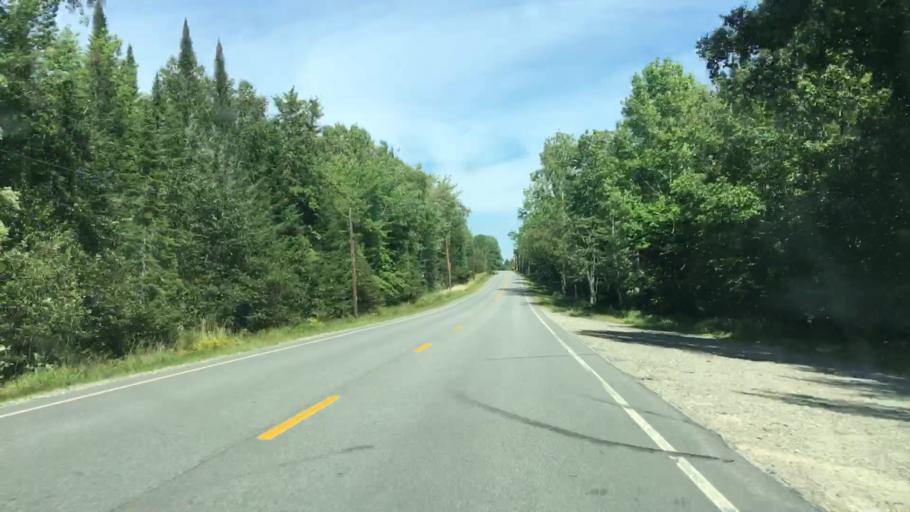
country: US
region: Maine
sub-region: Penobscot County
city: Howland
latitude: 45.2235
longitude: -68.7826
